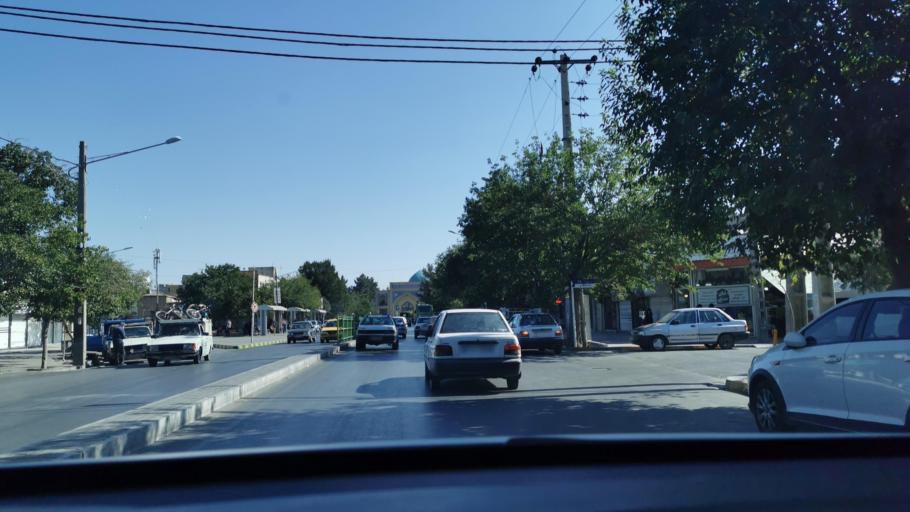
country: IR
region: Razavi Khorasan
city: Mashhad
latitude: 36.3394
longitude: 59.6271
